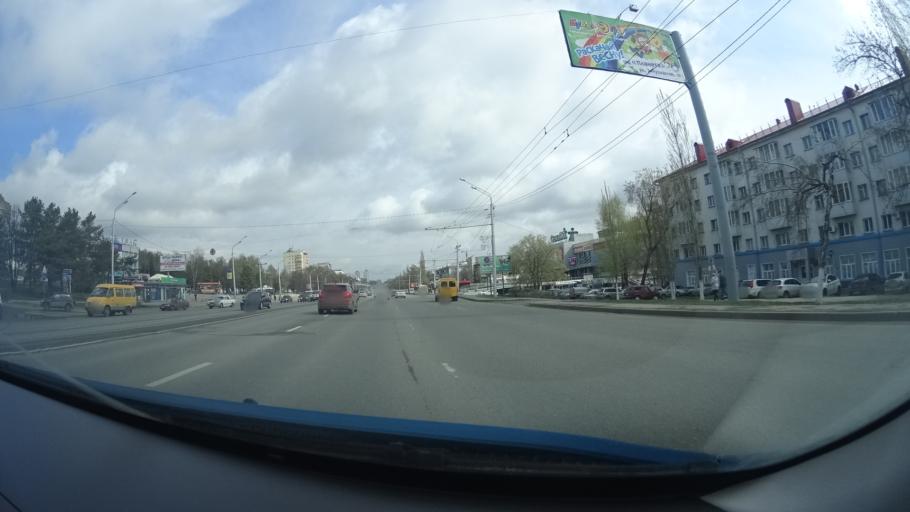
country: RU
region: Bashkortostan
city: Ufa
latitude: 54.7490
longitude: 55.9933
